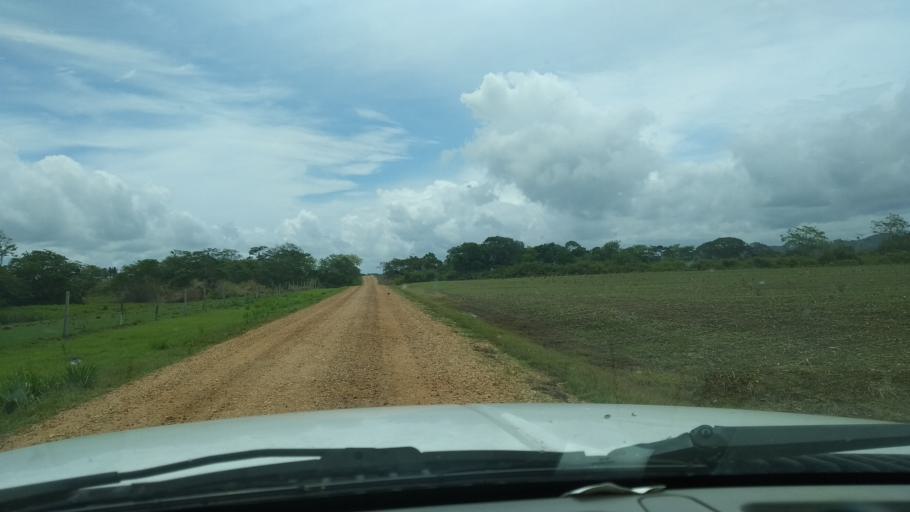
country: BZ
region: Cayo
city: San Ignacio
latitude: 17.2263
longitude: -88.9774
